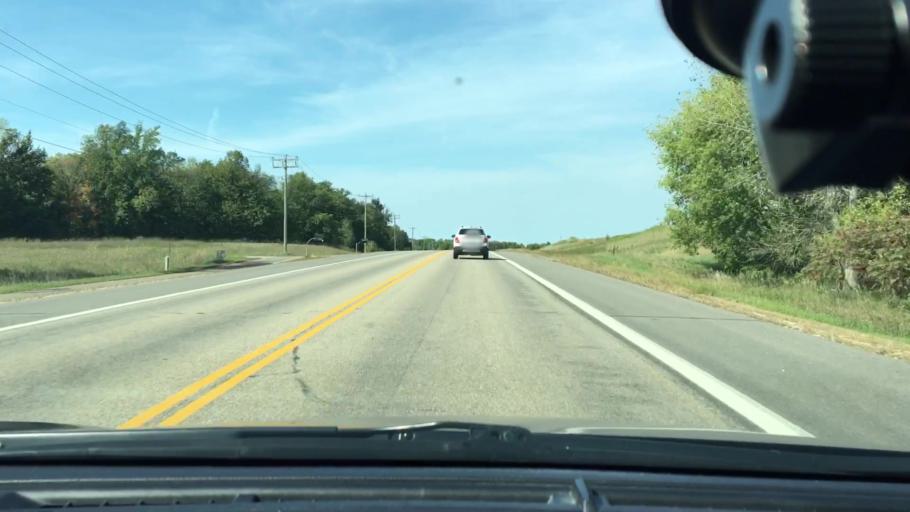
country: US
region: Minnesota
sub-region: Wright County
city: Hanover
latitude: 45.1629
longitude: -93.6700
